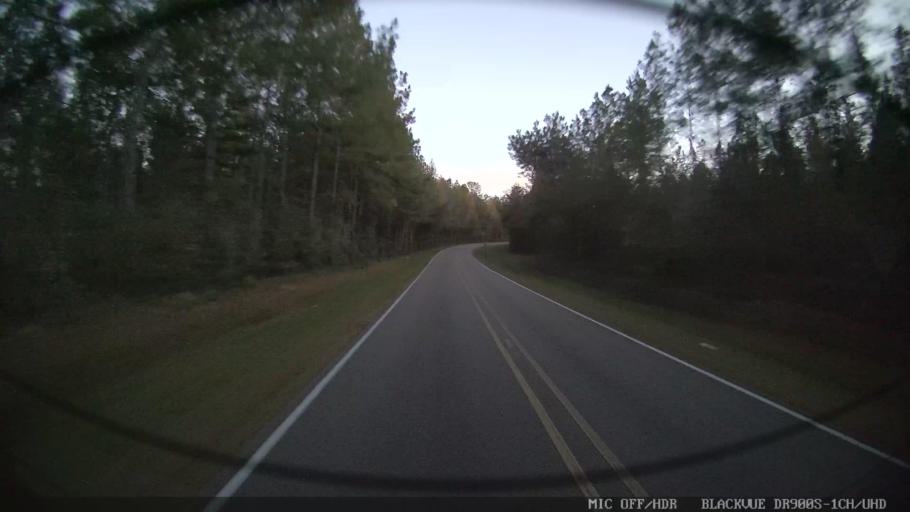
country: US
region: Mississippi
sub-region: Perry County
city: New Augusta
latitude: 31.0943
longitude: -89.1895
